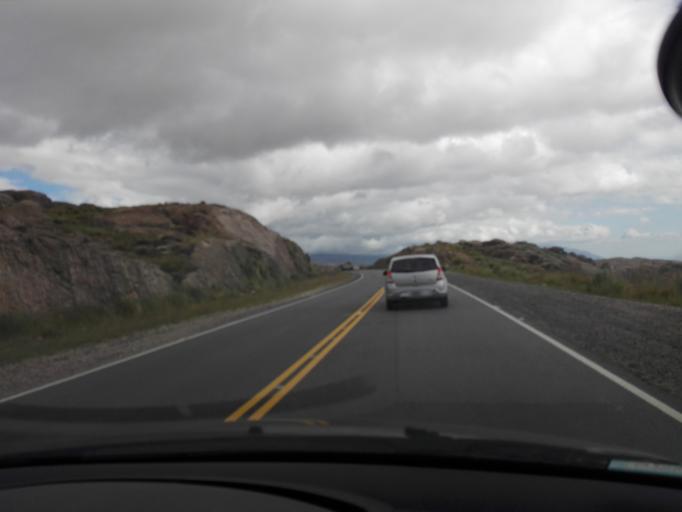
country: AR
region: Cordoba
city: Mina Clavero
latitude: -31.6368
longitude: -64.9079
